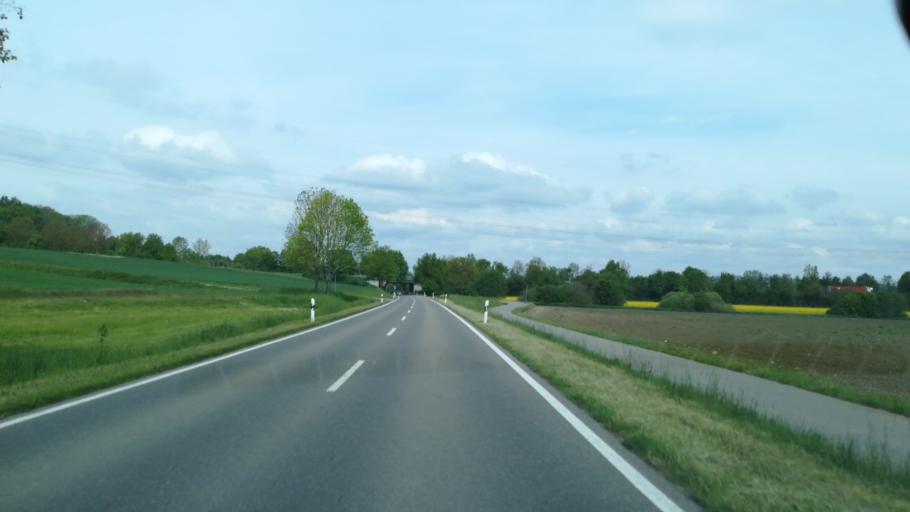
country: DE
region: Baden-Wuerttemberg
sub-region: Freiburg Region
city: Volkertshausen
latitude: 47.8109
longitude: 8.8730
